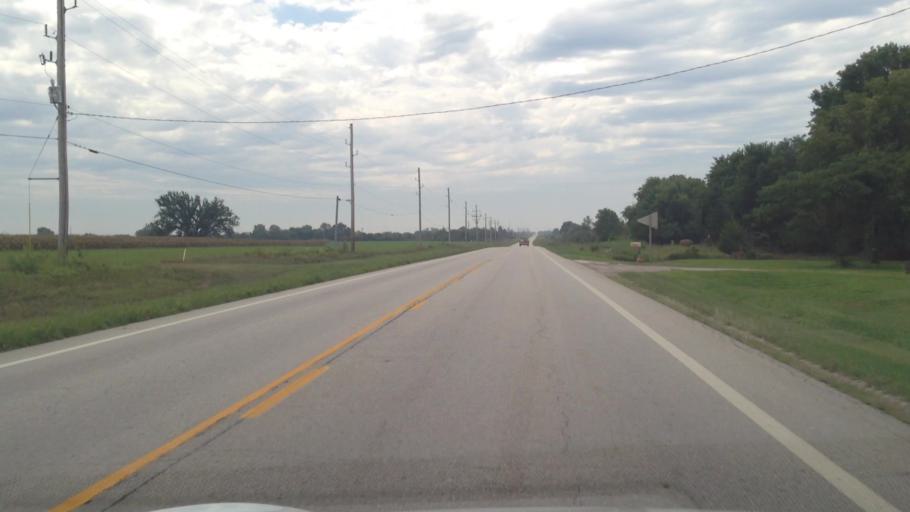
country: US
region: Kansas
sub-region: Allen County
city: Iola
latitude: 37.9568
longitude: -95.1701
